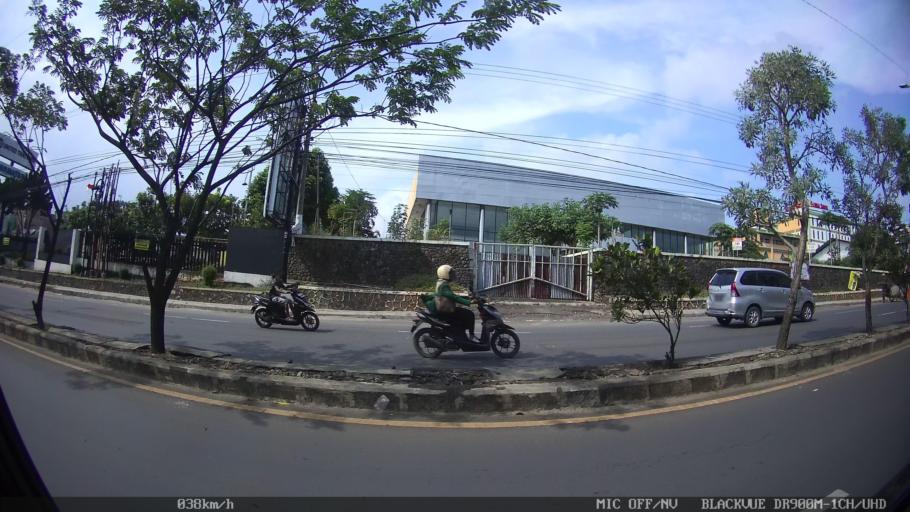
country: ID
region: Lampung
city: Kedaton
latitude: -5.3758
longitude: 105.2444
